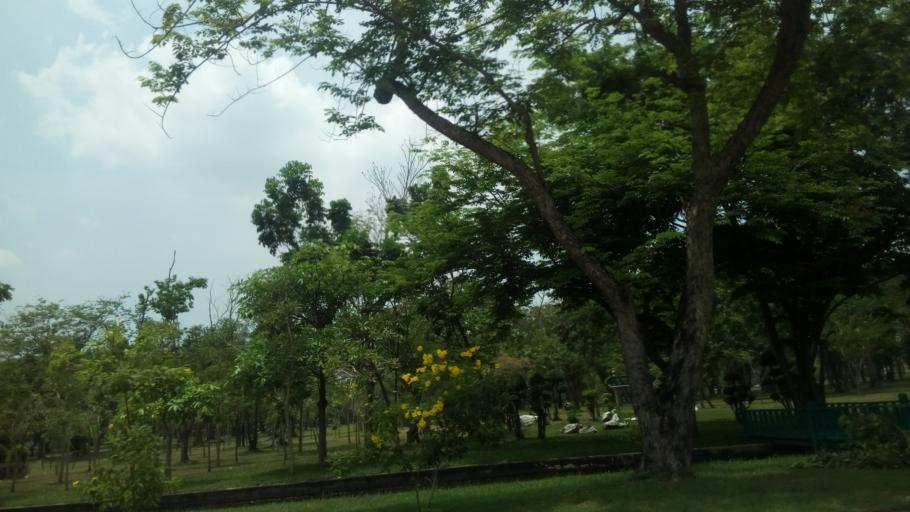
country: TH
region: Bangkok
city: Thawi Watthana
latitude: 13.7736
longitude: 100.3255
